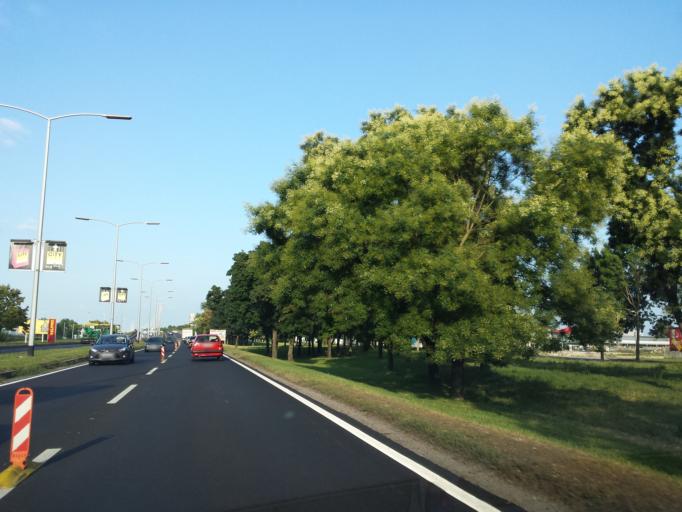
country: HR
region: Grad Zagreb
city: Dubrava
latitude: 45.7973
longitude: 16.0314
